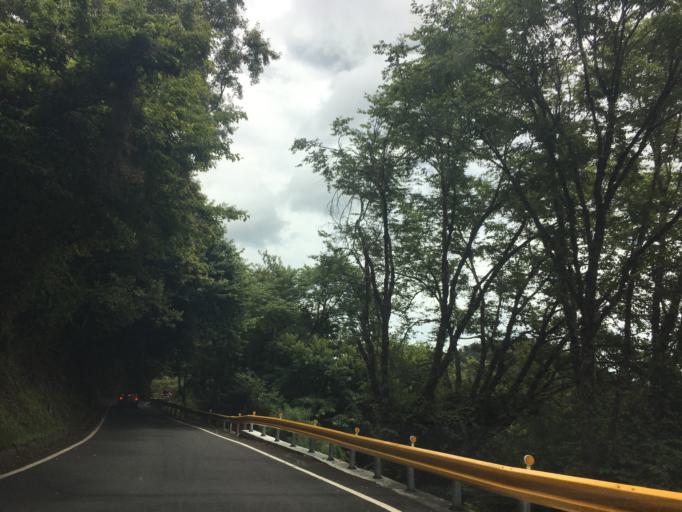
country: TW
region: Taiwan
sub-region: Hualien
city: Hualian
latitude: 24.1726
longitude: 121.3805
